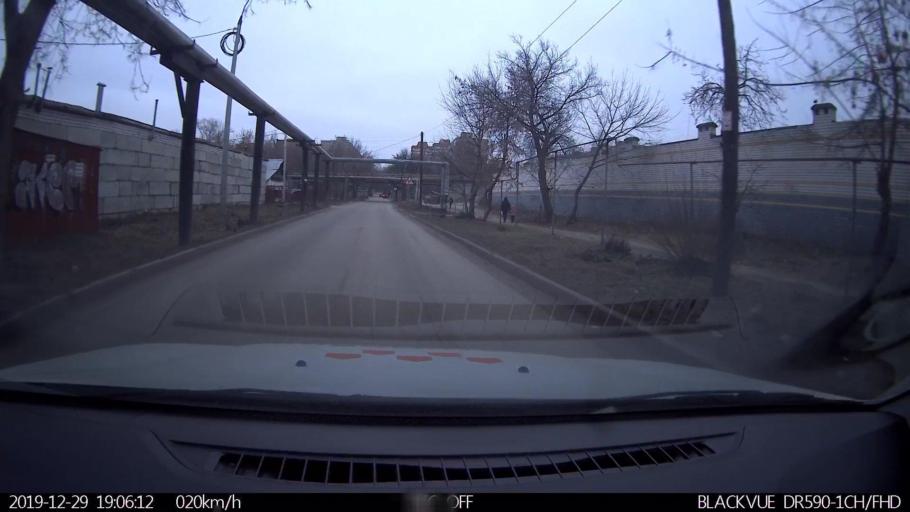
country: RU
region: Nizjnij Novgorod
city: Neklyudovo
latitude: 56.3571
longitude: 43.8610
